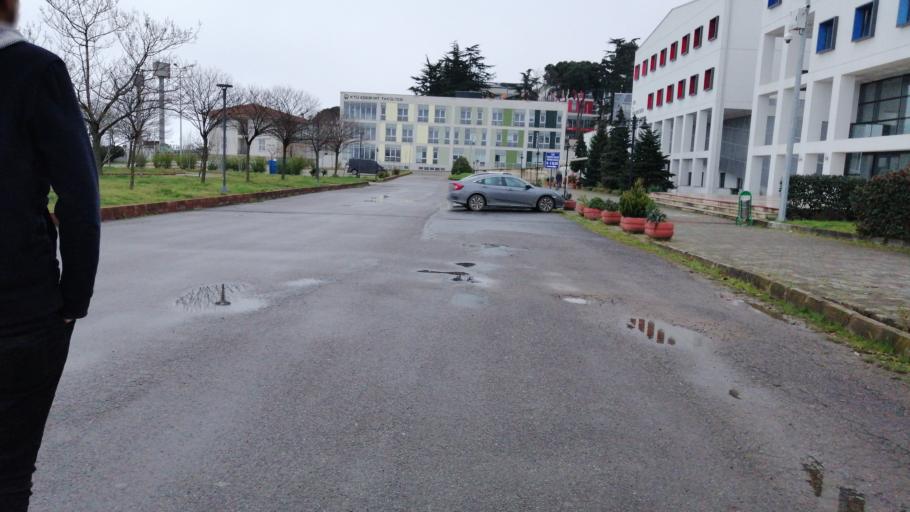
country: TR
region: Trabzon
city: Trabzon
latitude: 40.9992
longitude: 39.7674
